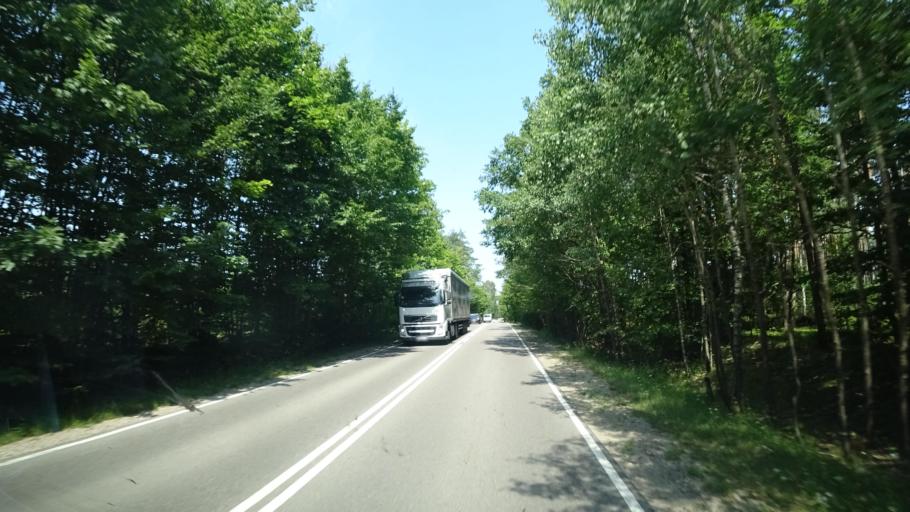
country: PL
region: Pomeranian Voivodeship
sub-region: Powiat koscierski
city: Dziemiany
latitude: 53.9896
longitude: 17.7689
